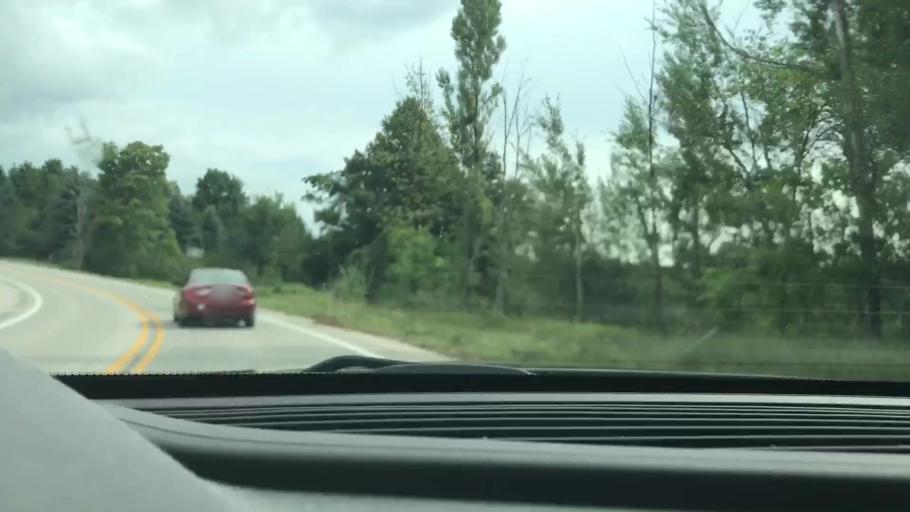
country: US
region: Michigan
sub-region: Antrim County
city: Bellaire
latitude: 45.0853
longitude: -85.2894
